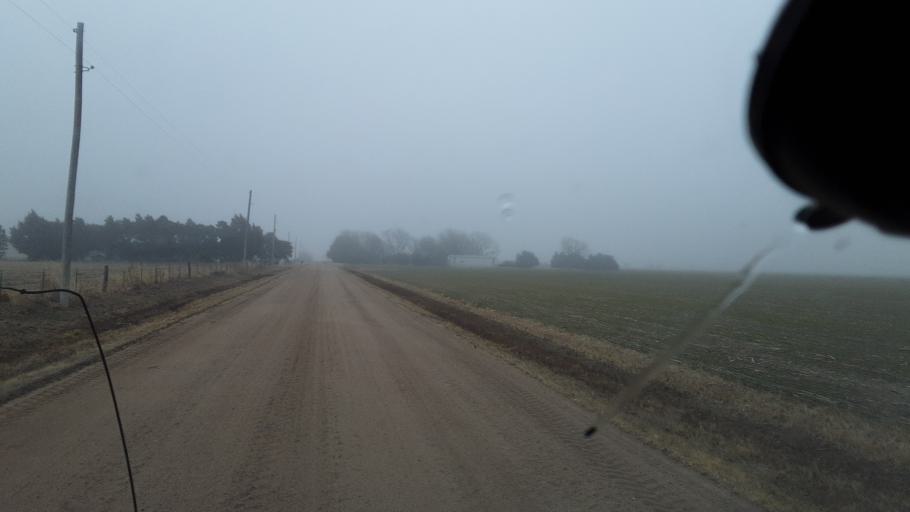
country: US
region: Kansas
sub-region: Reno County
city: South Hutchinson
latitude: 37.9845
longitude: -98.0065
